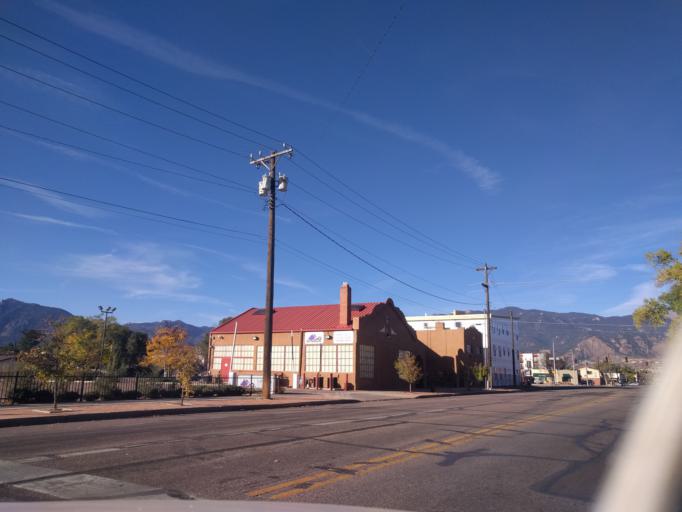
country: US
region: Colorado
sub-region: El Paso County
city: Colorado Springs
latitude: 38.8281
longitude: -104.8185
